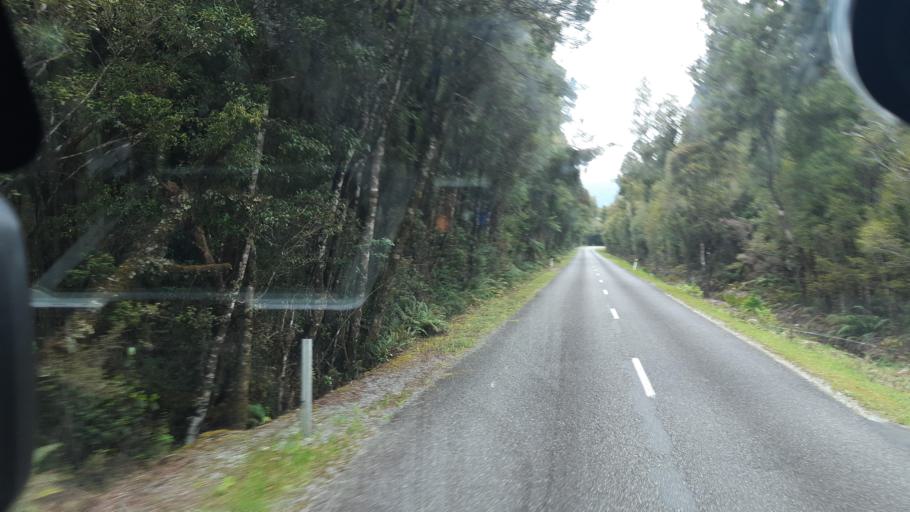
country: NZ
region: West Coast
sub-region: Westland District
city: Hokitika
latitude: -42.7852
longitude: 171.1197
